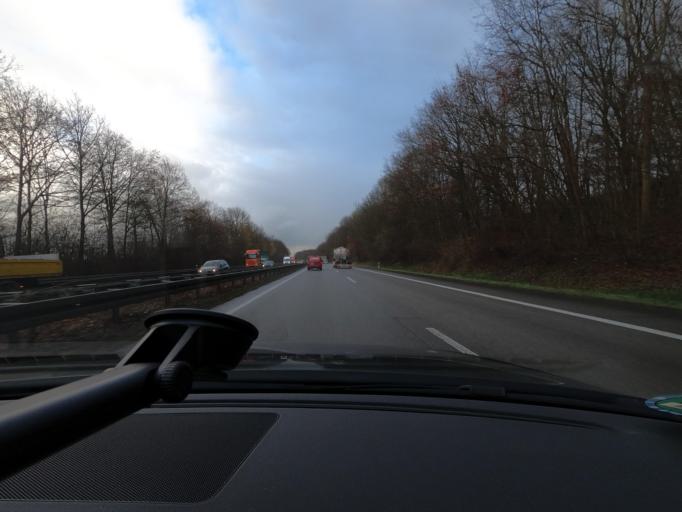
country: DE
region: North Rhine-Westphalia
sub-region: Regierungsbezirk Arnsberg
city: Frondenberg
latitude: 51.5245
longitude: 7.7778
